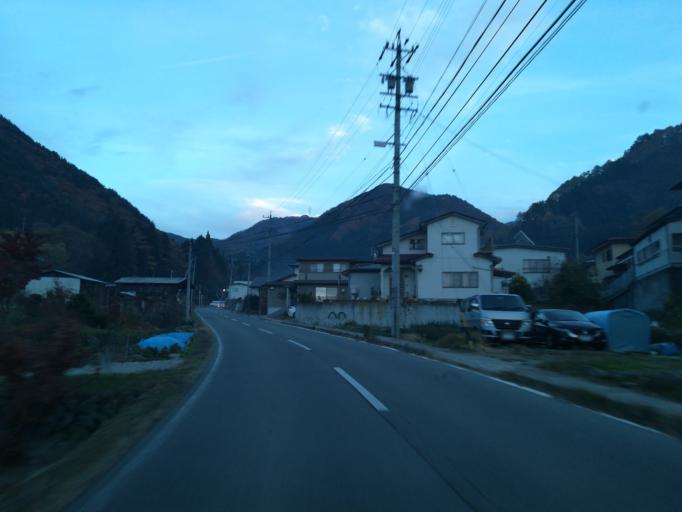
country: JP
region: Nagano
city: Suzaka
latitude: 36.5832
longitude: 138.2736
